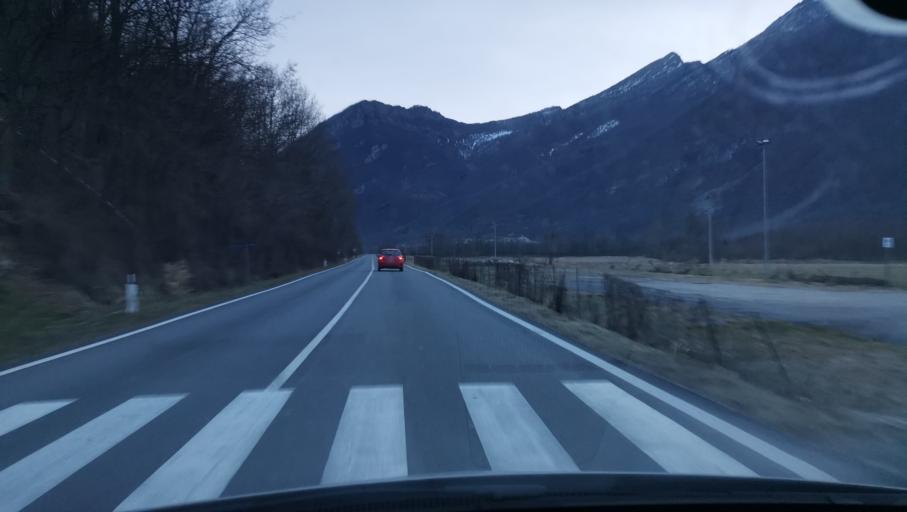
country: IT
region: Piedmont
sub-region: Provincia di Cuneo
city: Valloriate
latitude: 44.3113
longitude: 7.3562
